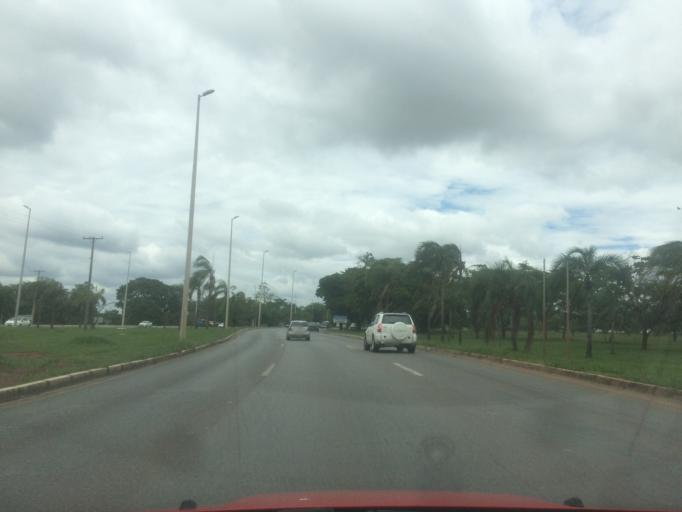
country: BR
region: Federal District
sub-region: Brasilia
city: Brasilia
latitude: -15.8052
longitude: -47.8548
